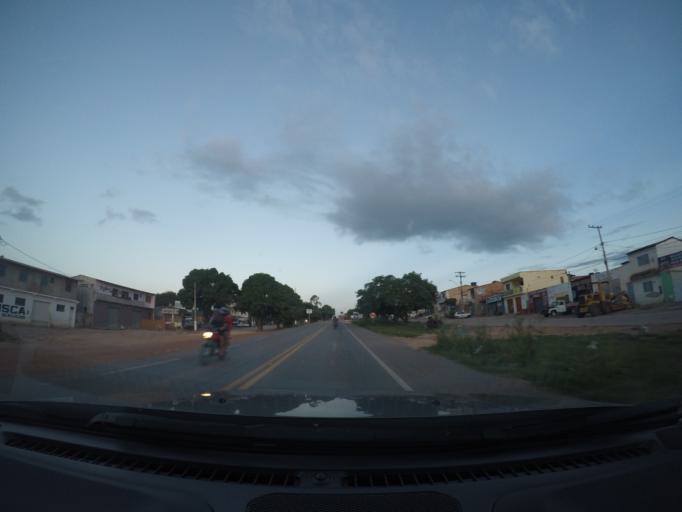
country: BR
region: Bahia
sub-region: Seabra
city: Seabra
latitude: -12.4282
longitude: -41.7753
